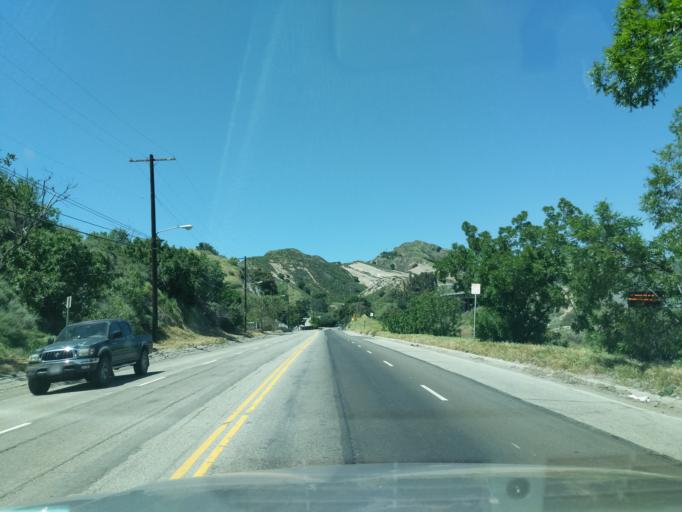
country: US
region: California
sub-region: Los Angeles County
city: San Fernando
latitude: 34.3220
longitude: -118.5007
